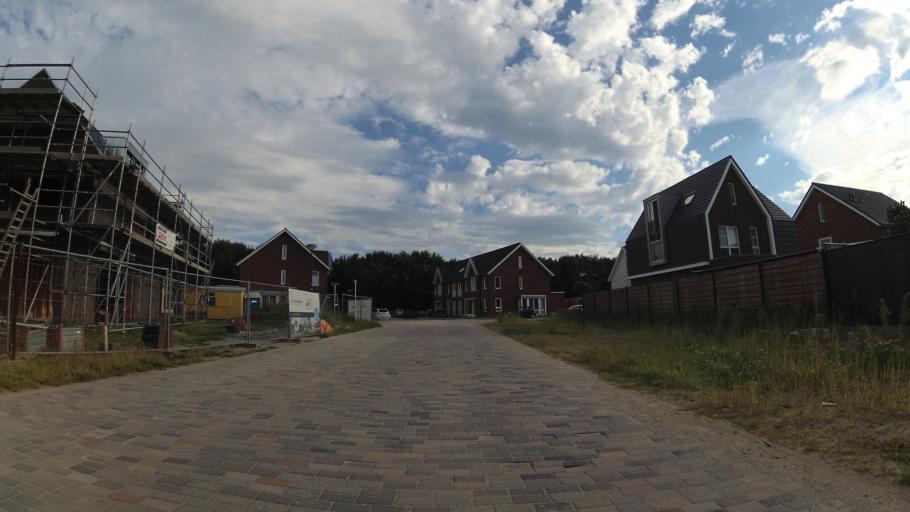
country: NL
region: North Brabant
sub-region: Gemeente Oosterhout
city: Oosterhout
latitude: 51.6484
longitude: 4.8233
